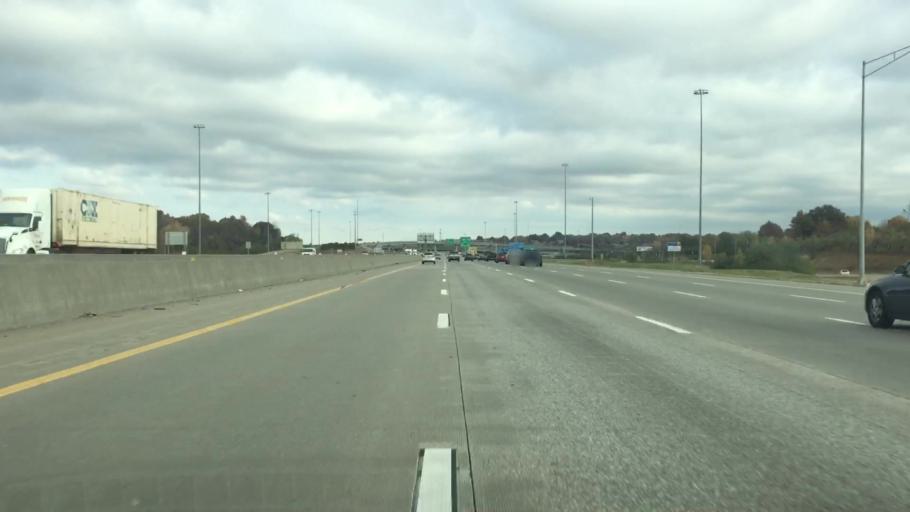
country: US
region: Missouri
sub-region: Jackson County
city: Grandview
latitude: 38.9207
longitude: -94.5277
